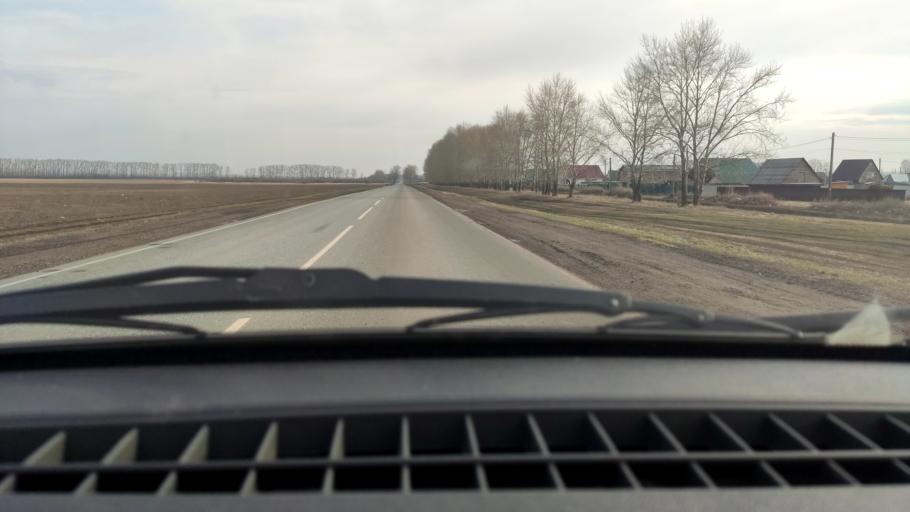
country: RU
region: Bashkortostan
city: Davlekanovo
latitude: 54.3933
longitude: 55.2053
